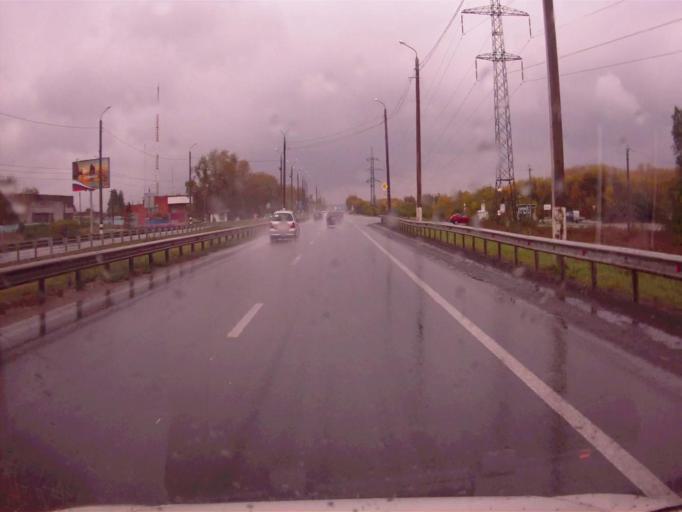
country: RU
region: Chelyabinsk
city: Dolgoderevenskoye
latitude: 55.2544
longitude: 61.3534
